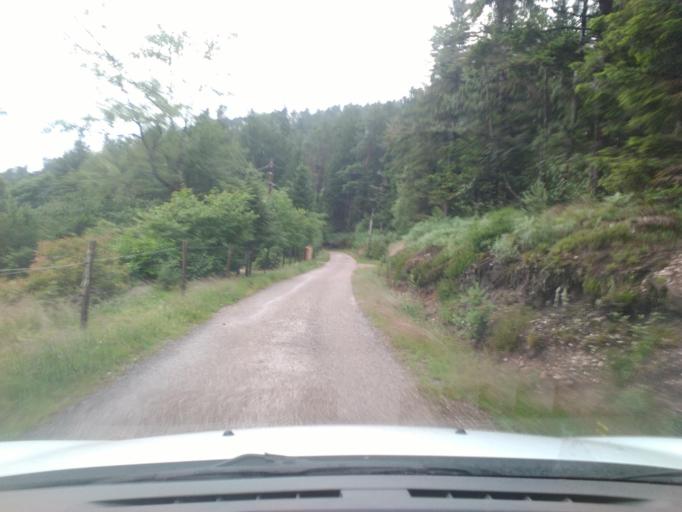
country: FR
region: Lorraine
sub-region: Departement des Vosges
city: Le Tholy
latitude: 48.1065
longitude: 6.7124
